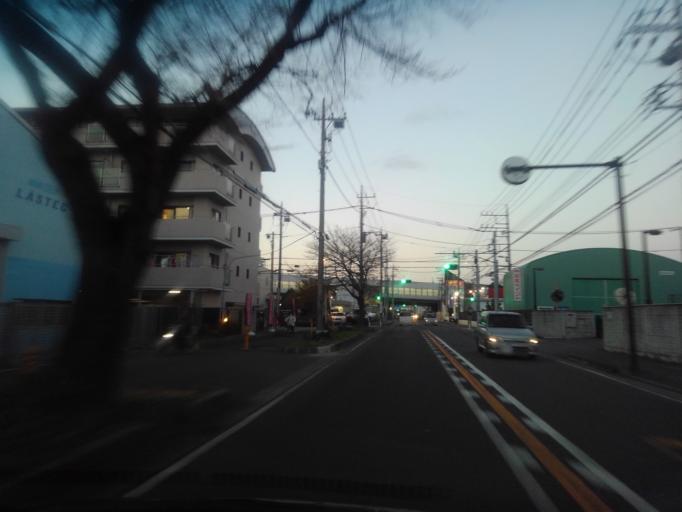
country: JP
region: Kanagawa
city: Minami-rinkan
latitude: 35.4834
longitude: 139.4643
